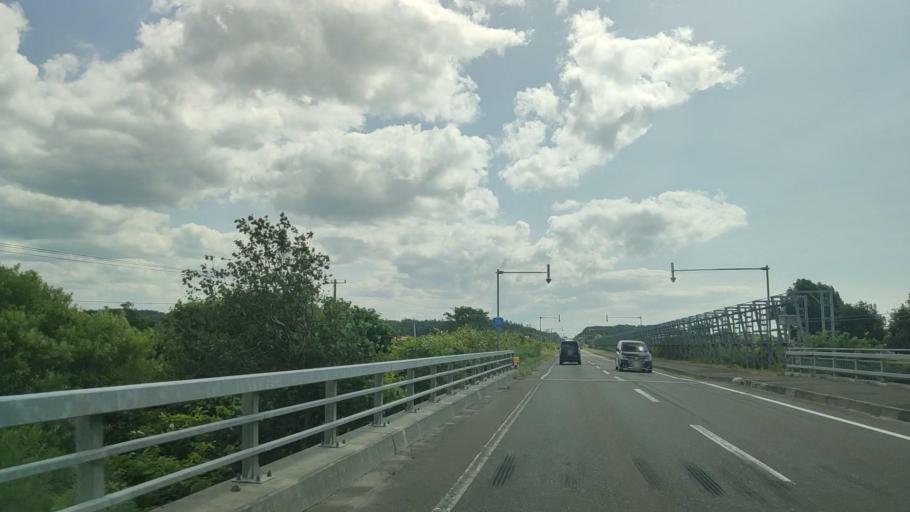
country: JP
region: Hokkaido
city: Makubetsu
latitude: 44.7736
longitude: 141.7921
